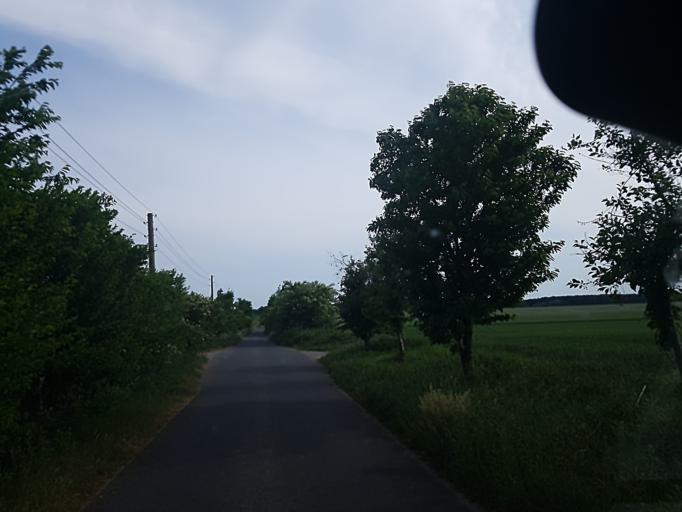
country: DE
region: Brandenburg
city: Niemegk
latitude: 52.0107
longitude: 12.6623
